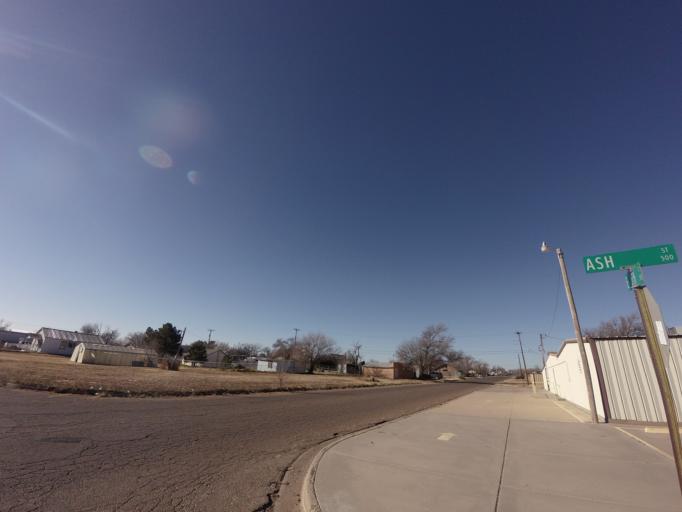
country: US
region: New Mexico
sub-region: Curry County
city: Clovis
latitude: 34.4030
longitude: -103.1902
